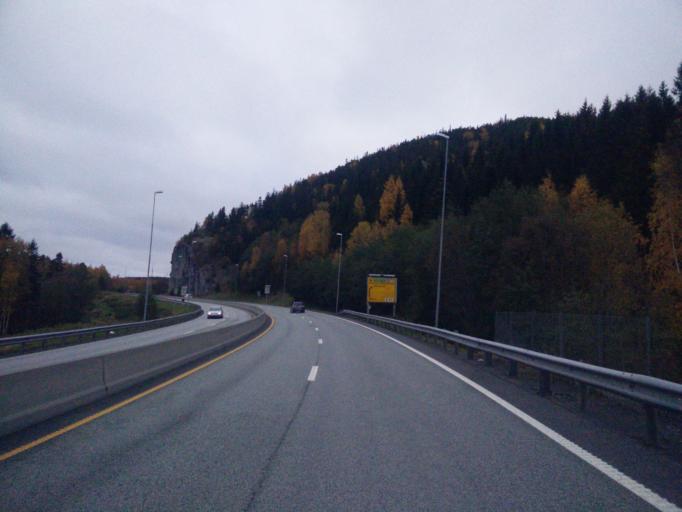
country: NO
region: Sor-Trondelag
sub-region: Malvik
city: Hommelvik
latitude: 63.4061
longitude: 10.8169
